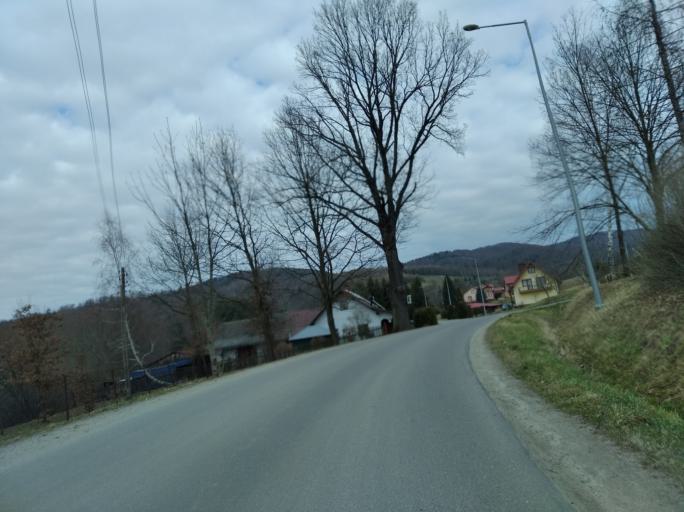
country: PL
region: Subcarpathian Voivodeship
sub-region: Powiat strzyzowski
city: Frysztak
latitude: 49.8429
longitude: 21.6249
